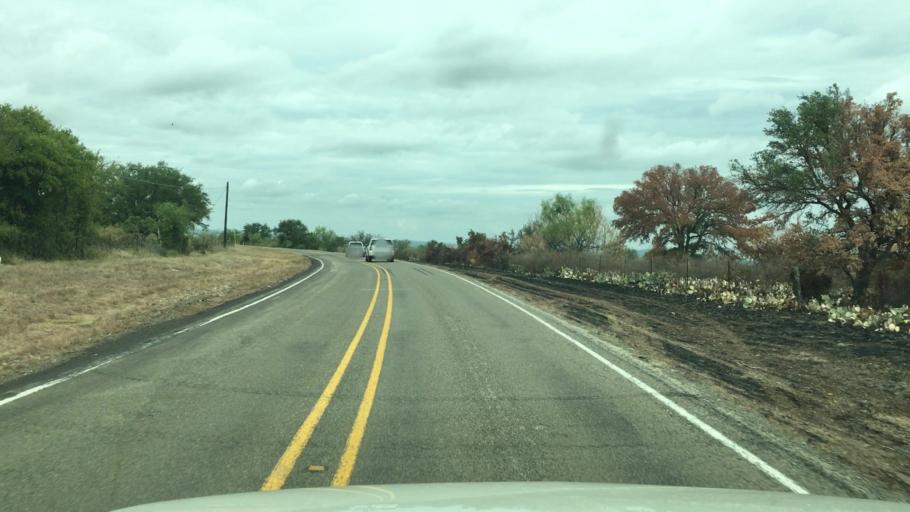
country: US
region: Texas
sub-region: Llano County
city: Horseshoe Bay
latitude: 30.4867
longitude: -98.4315
